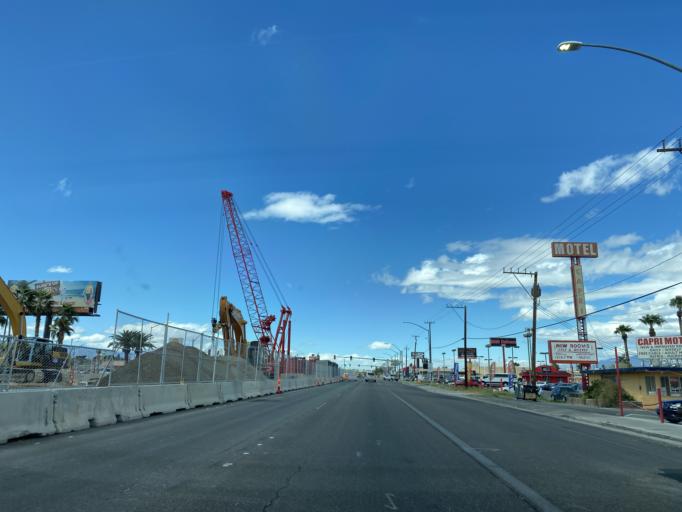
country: US
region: Nevada
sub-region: Clark County
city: Winchester
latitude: 36.1477
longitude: -115.1035
